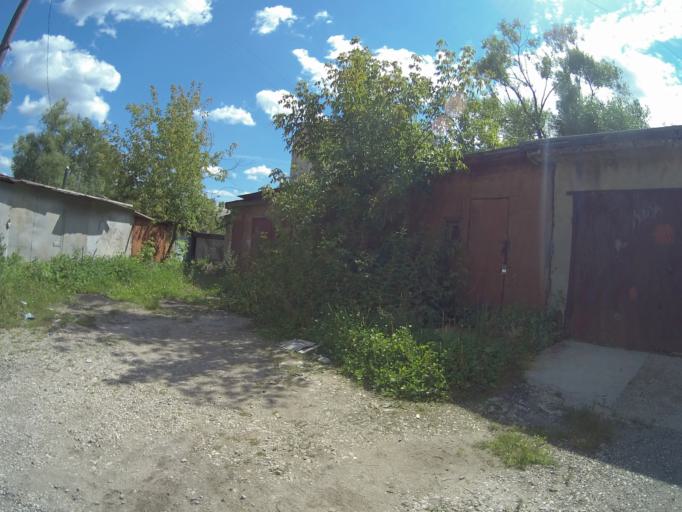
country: RU
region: Vladimir
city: Vladimir
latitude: 56.1384
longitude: 40.4173
